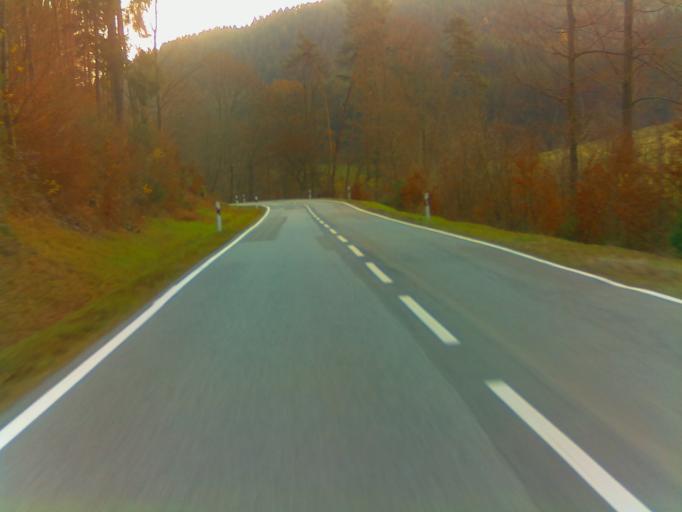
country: DE
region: Hesse
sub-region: Regierungsbezirk Darmstadt
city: Hesseneck
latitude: 49.5803
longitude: 9.0466
